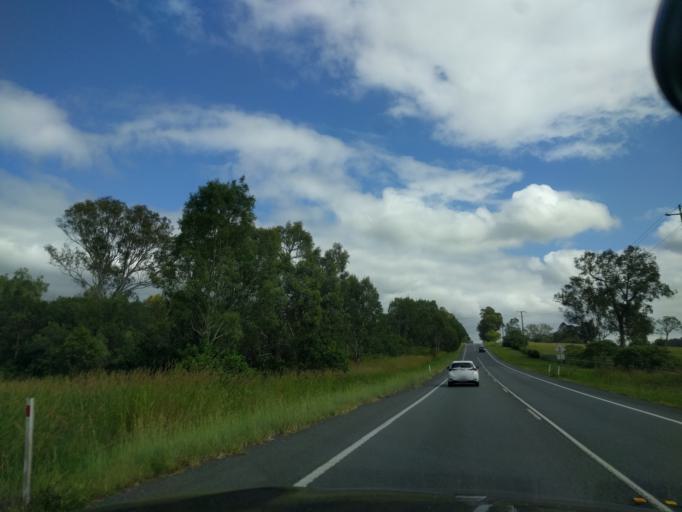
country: AU
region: Queensland
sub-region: Logan
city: Cedar Vale
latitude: -27.9052
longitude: 152.9759
